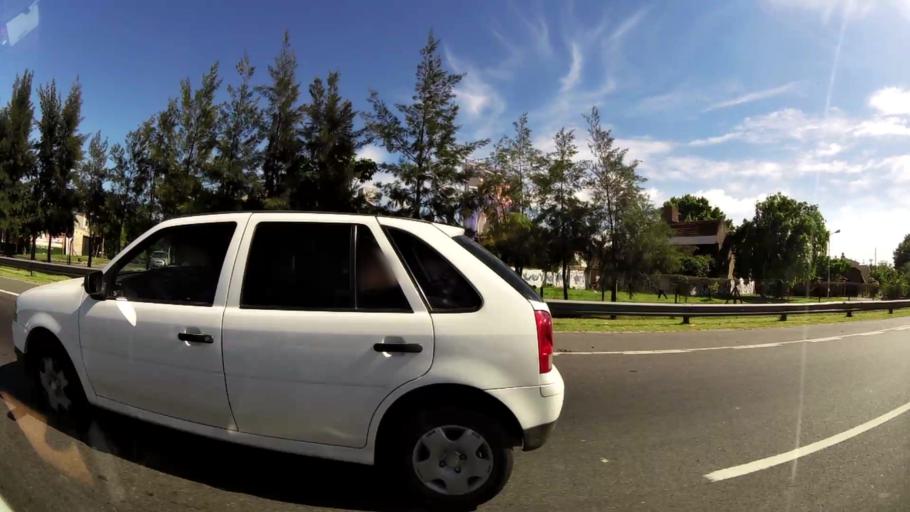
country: AR
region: Buenos Aires
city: Caseros
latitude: -34.6310
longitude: -58.5830
